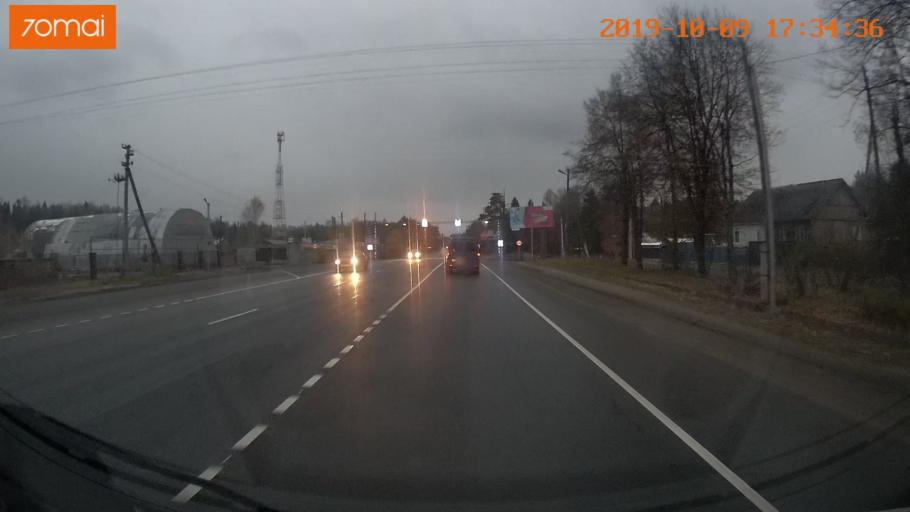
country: RU
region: Ivanovo
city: Bogorodskoye
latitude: 57.1051
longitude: 41.0102
